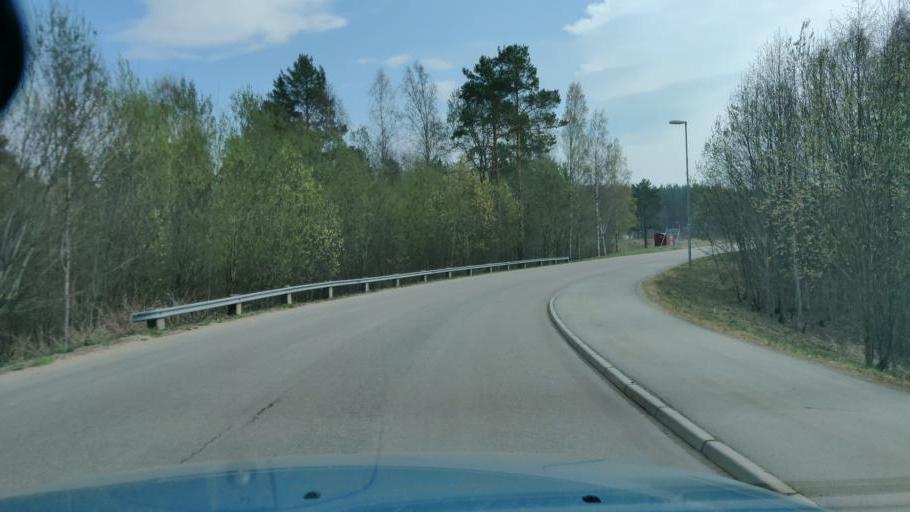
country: SE
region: Vaermland
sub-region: Munkfors Kommun
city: Munkfors
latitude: 59.8388
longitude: 13.5463
